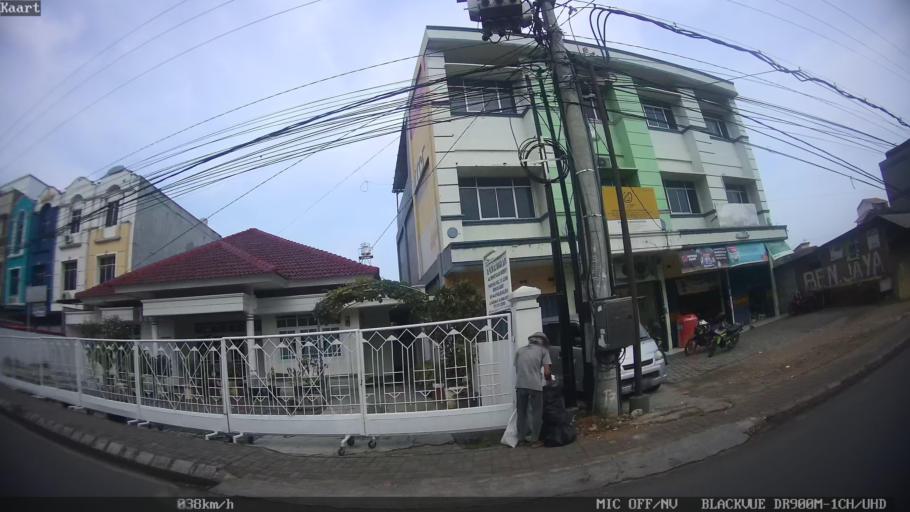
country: ID
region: Lampung
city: Bandarlampung
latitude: -5.4143
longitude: 105.2664
